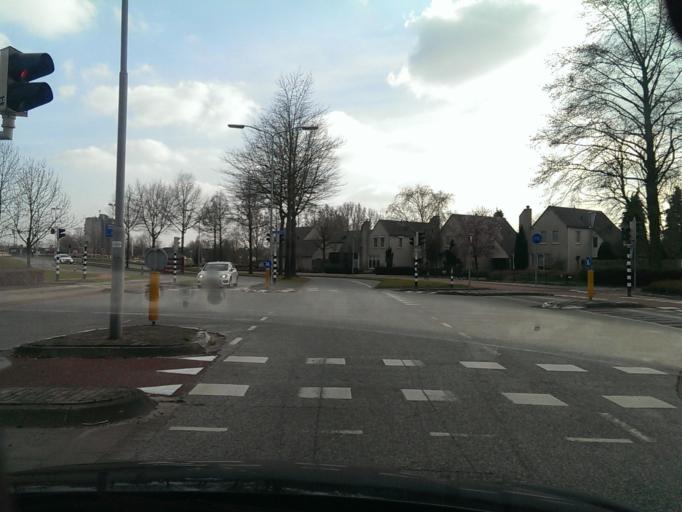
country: NL
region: North Brabant
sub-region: Gemeente Veldhoven
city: Veldhoven
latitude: 51.4262
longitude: 5.4035
